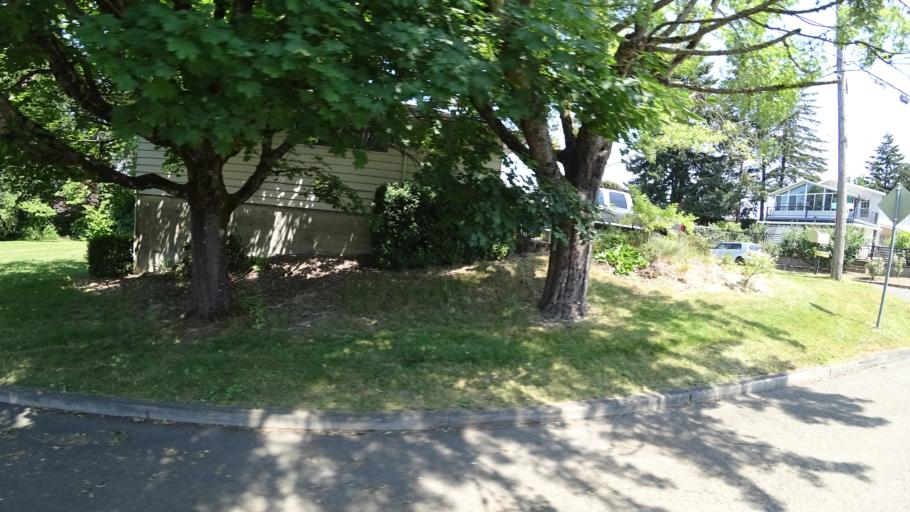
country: US
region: Oregon
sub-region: Multnomah County
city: Lents
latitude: 45.4586
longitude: -122.5704
